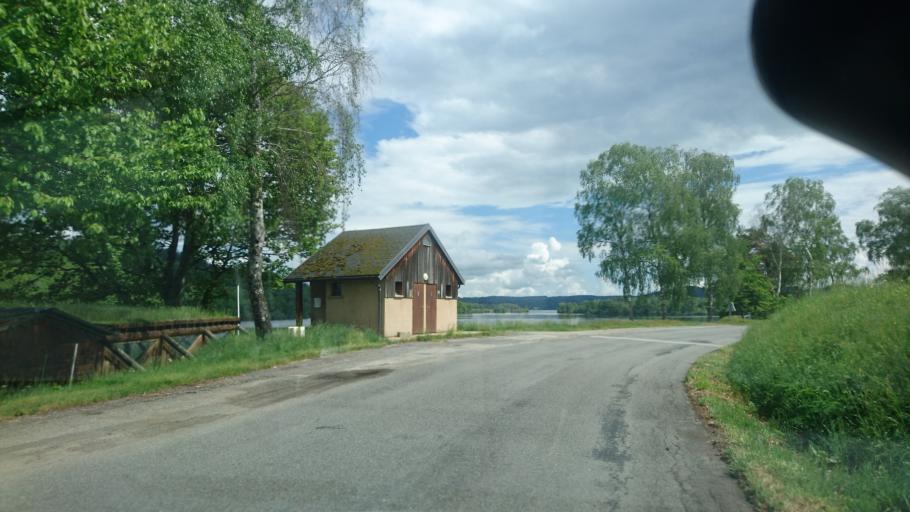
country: FR
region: Limousin
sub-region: Departement de la Haute-Vienne
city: Peyrat-le-Chateau
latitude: 45.7893
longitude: 1.8829
